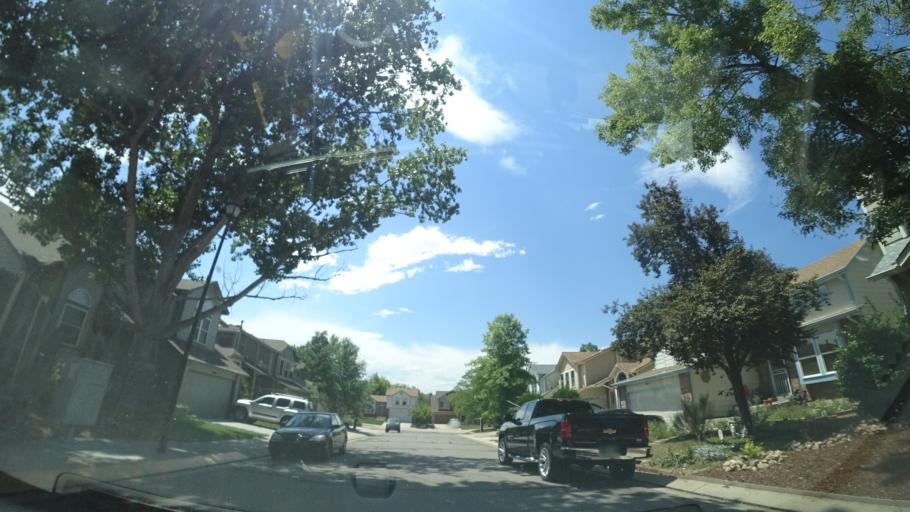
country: US
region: Colorado
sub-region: Jefferson County
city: Lakewood
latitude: 39.6960
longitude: -105.0976
